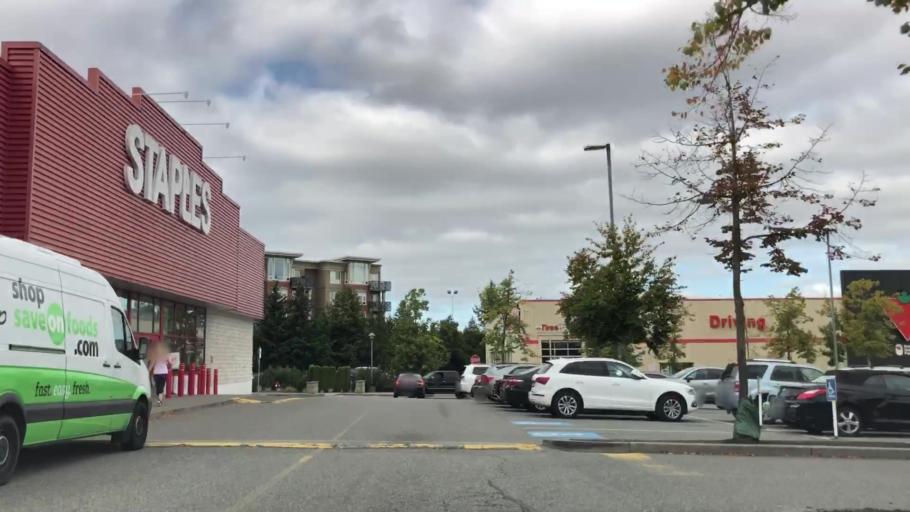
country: CA
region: British Columbia
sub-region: Greater Vancouver Regional District
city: White Rock
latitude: 49.0569
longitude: -122.8031
